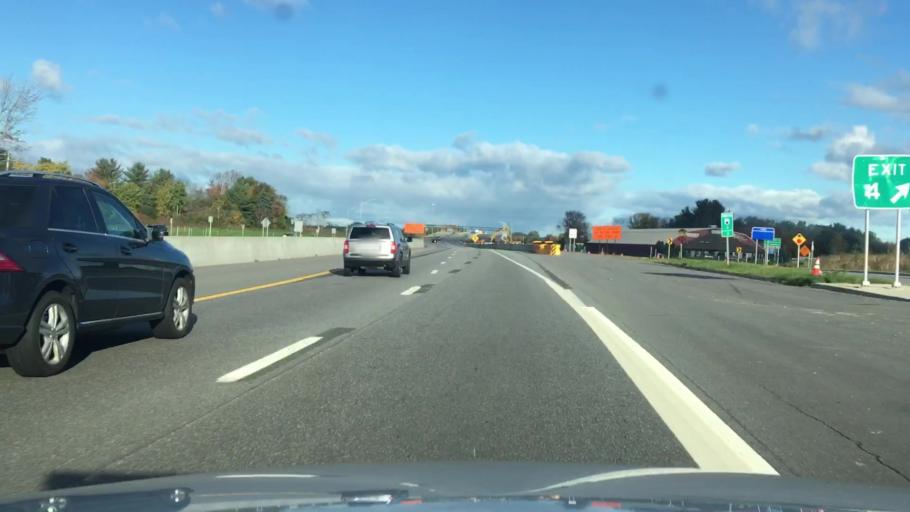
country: US
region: Maine
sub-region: York County
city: South Eliot
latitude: 43.1123
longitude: -70.8183
